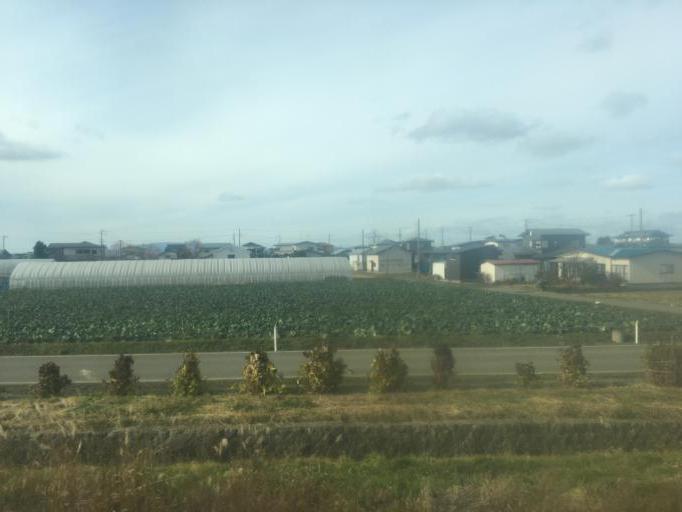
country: JP
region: Akita
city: Tenno
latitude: 39.8961
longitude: 140.0722
